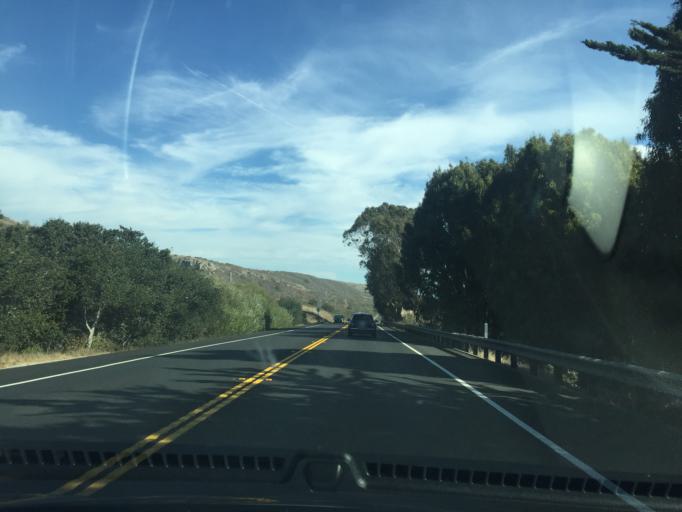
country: US
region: California
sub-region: Santa Cruz County
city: Bonny Doon
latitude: 36.9824
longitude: -122.1430
